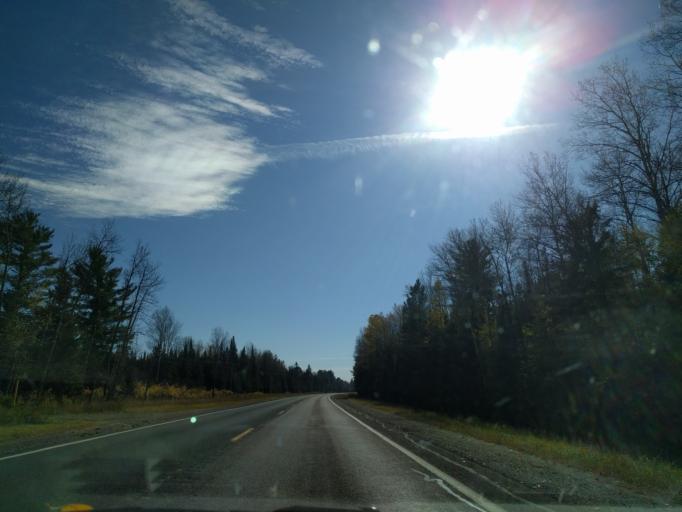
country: US
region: Michigan
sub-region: Marquette County
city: West Ishpeming
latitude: 46.3252
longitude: -87.9697
